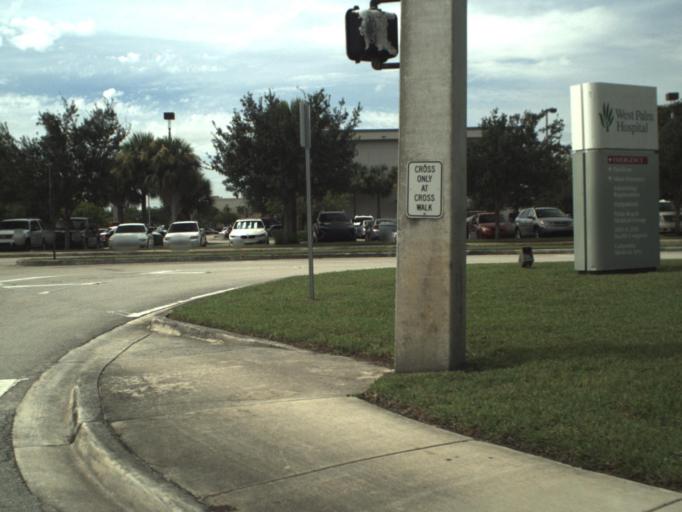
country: US
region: Florida
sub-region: Palm Beach County
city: Mangonia Park
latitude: 26.7627
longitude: -80.0868
